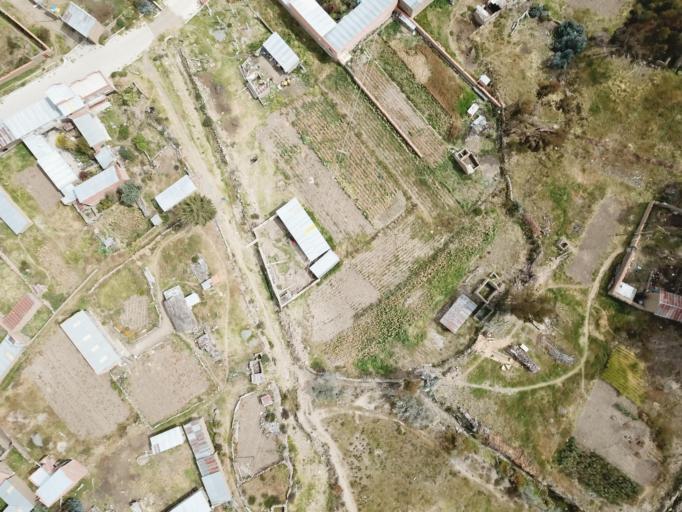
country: BO
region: La Paz
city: Achacachi
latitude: -16.0519
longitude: -68.8145
